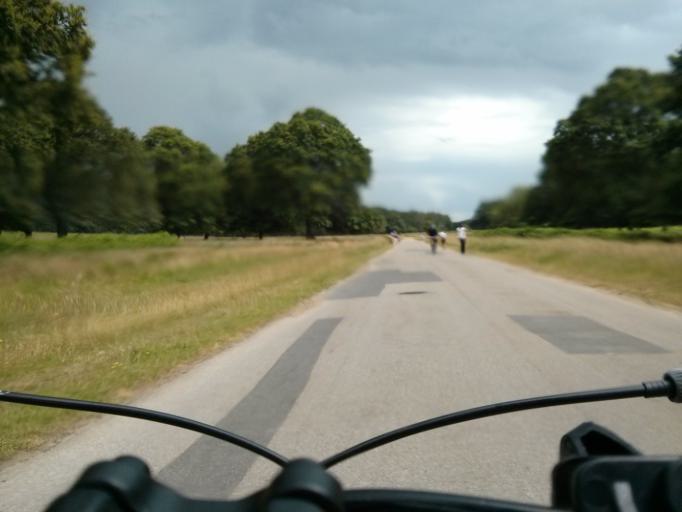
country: GB
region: England
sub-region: Greater London
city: Kingston upon Thames
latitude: 51.4344
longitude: -0.2843
